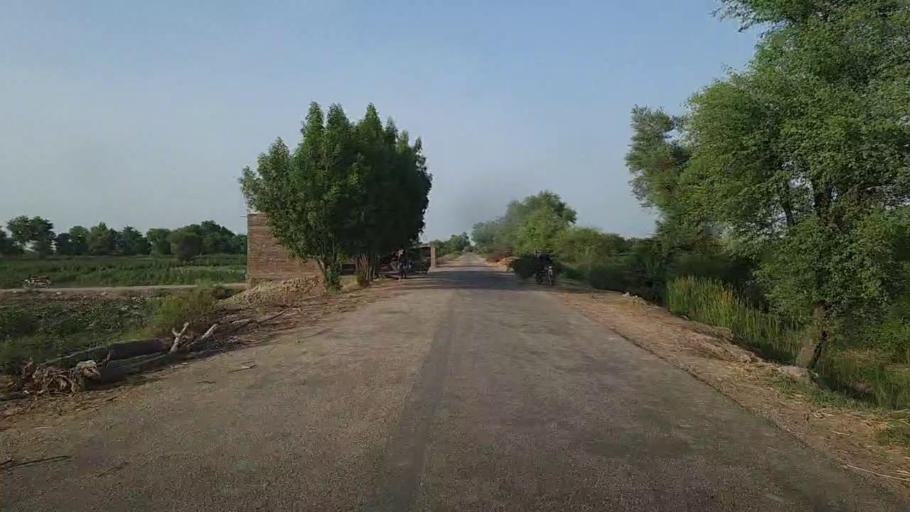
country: PK
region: Sindh
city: Ubauro
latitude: 28.1084
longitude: 69.8169
